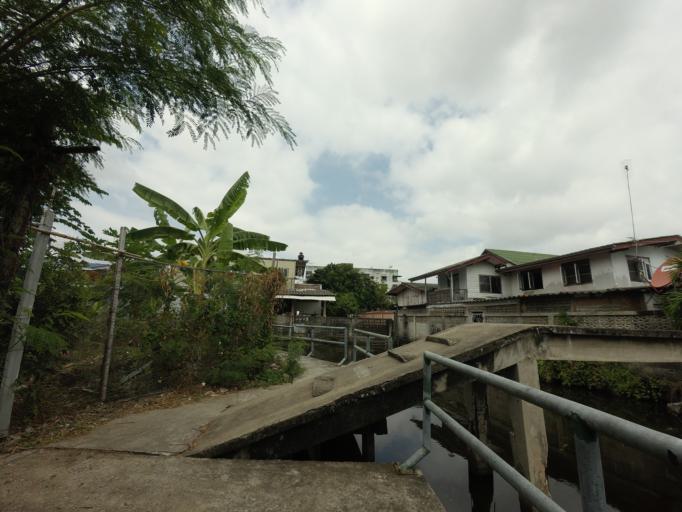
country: TH
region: Bangkok
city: Thung Khru
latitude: 13.6398
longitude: 100.4961
